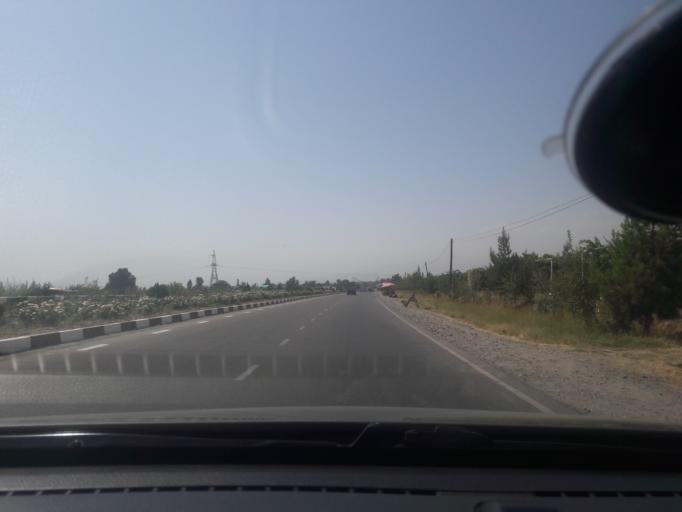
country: TJ
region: Republican Subordination
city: Hisor
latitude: 38.5599
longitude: 68.4552
